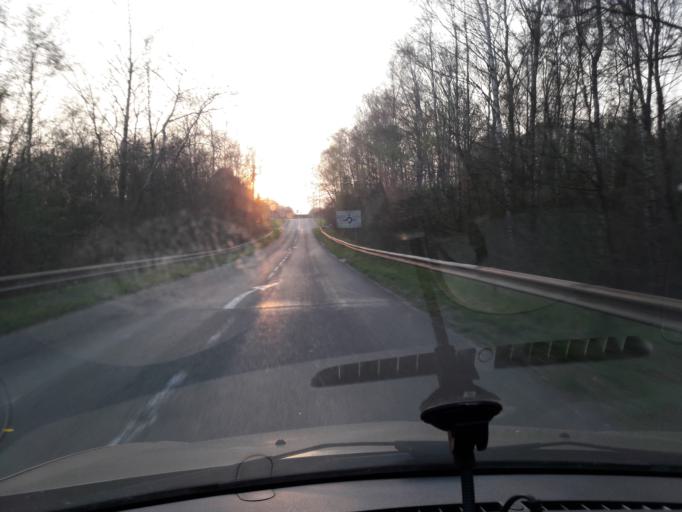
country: FR
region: Nord-Pas-de-Calais
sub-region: Departement du Nord
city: Recquignies
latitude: 50.2761
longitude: 4.0371
